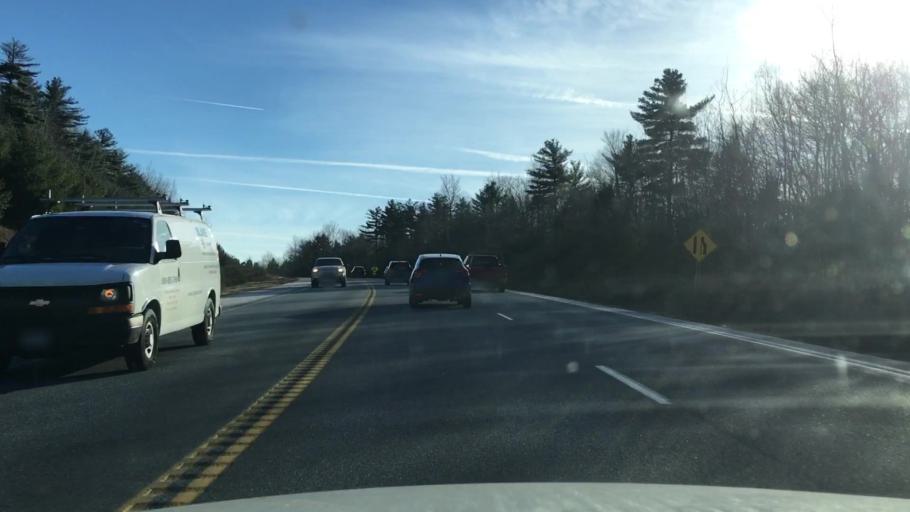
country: US
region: Maine
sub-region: Hancock County
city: Dedham
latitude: 44.6740
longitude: -68.5784
